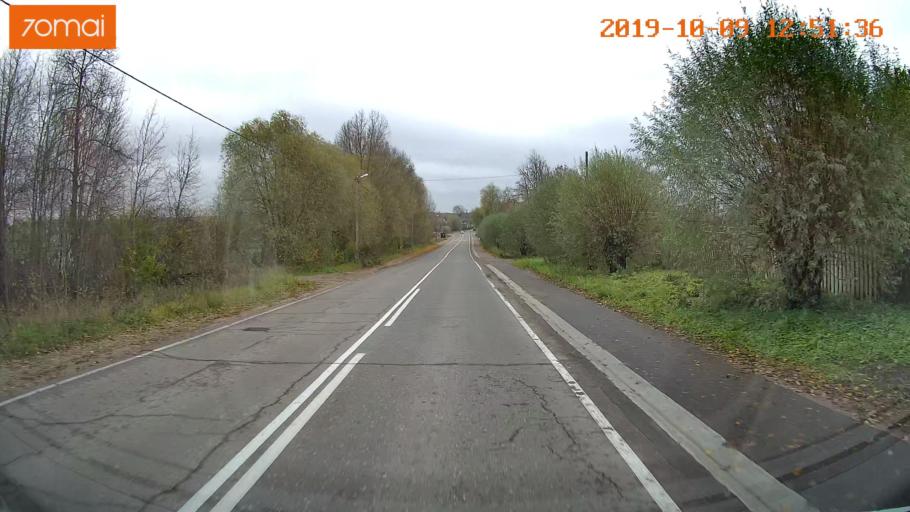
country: RU
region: Jaroslavl
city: Prechistoye
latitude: 58.4187
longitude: 40.3438
